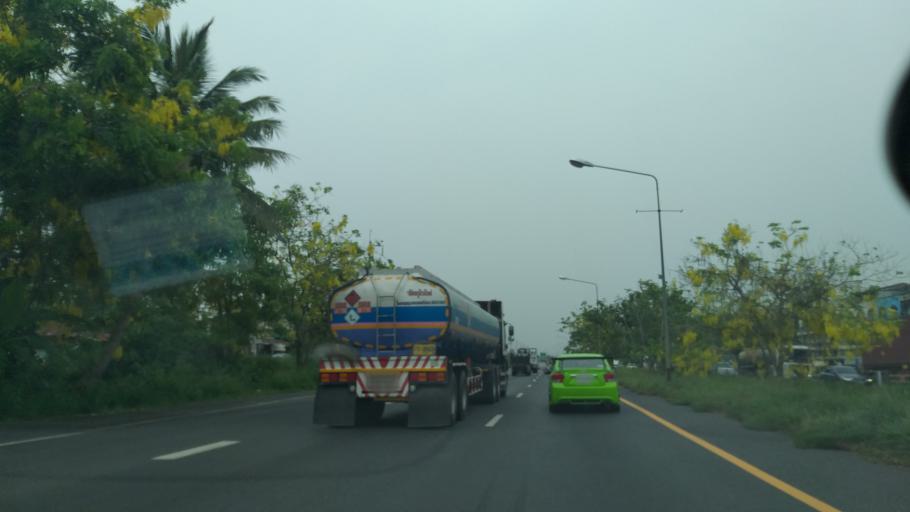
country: TH
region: Chon Buri
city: Ko Chan
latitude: 13.3902
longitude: 101.2796
